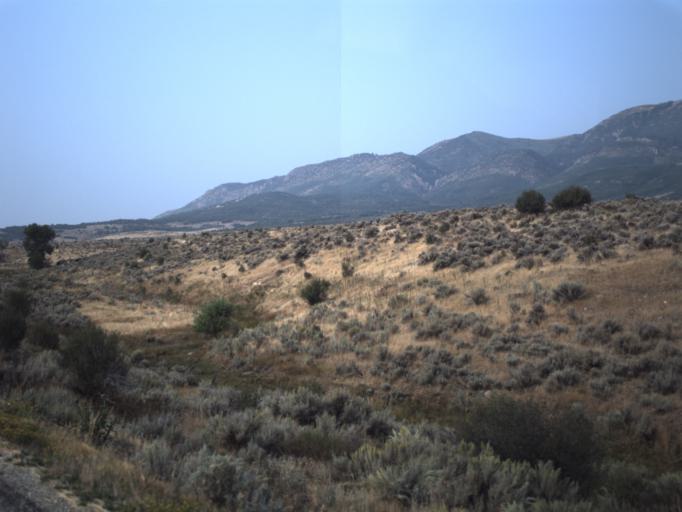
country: US
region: Utah
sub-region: Summit County
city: Coalville
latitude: 40.9705
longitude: -111.5404
